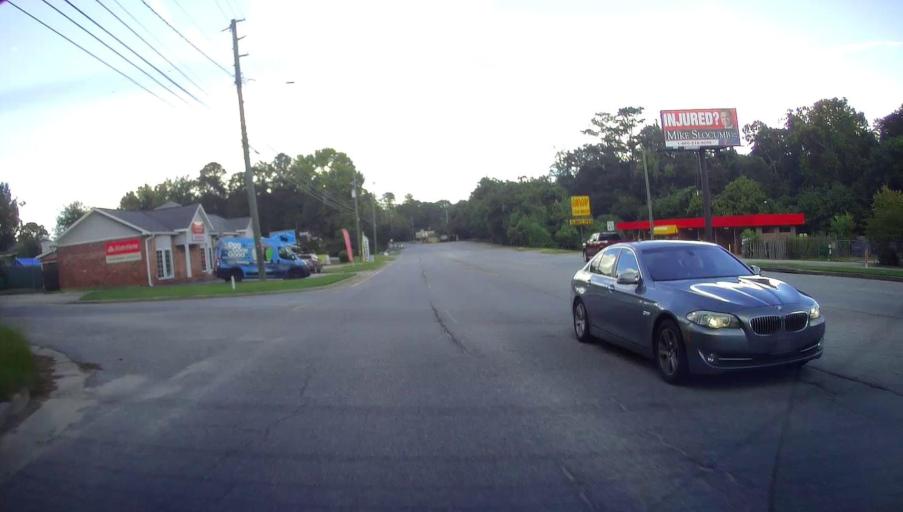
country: US
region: Georgia
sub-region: Muscogee County
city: Columbus
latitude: 32.5291
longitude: -84.9116
